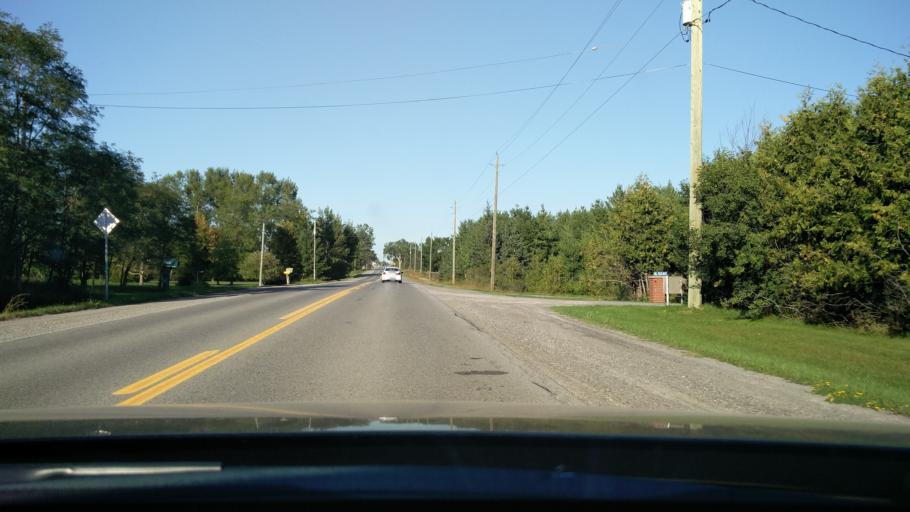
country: CA
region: Ontario
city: Carleton Place
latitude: 45.1222
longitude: -75.9536
